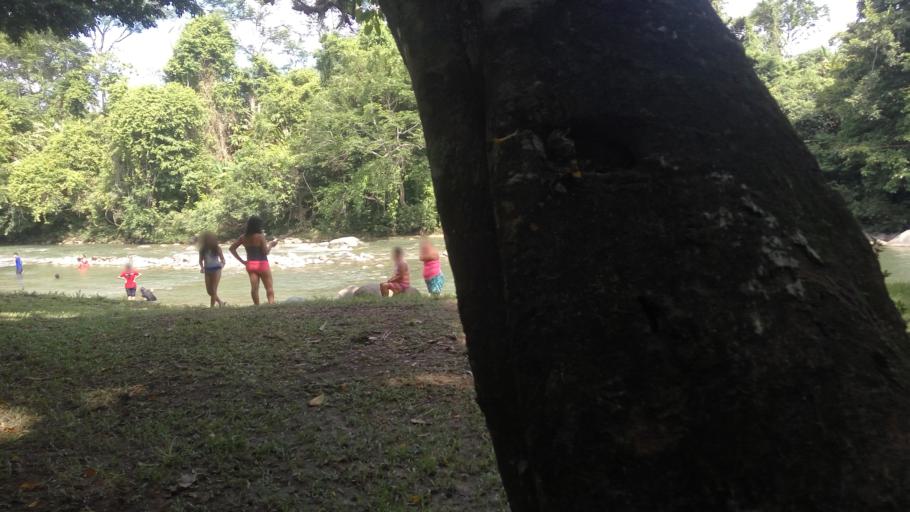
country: MX
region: Tabasco
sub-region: Teapa
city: Eureka y Belen
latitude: 17.5535
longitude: -92.9242
